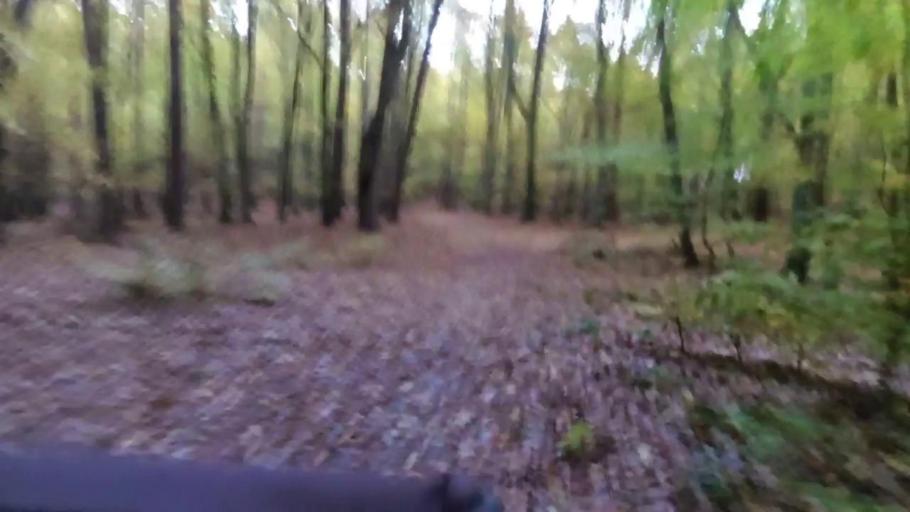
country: PL
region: West Pomeranian Voivodeship
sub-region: Powiat kamienski
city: Miedzyzdroje
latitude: 53.8657
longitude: 14.4501
